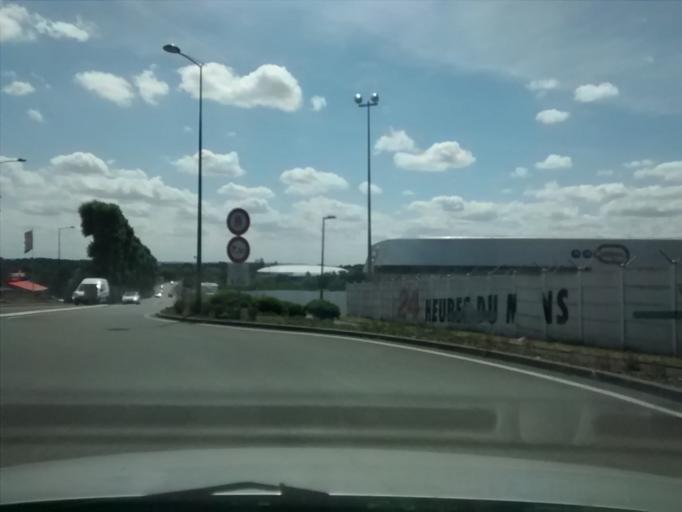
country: FR
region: Pays de la Loire
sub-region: Departement de la Sarthe
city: Le Mans
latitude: 47.9619
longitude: 0.2230
